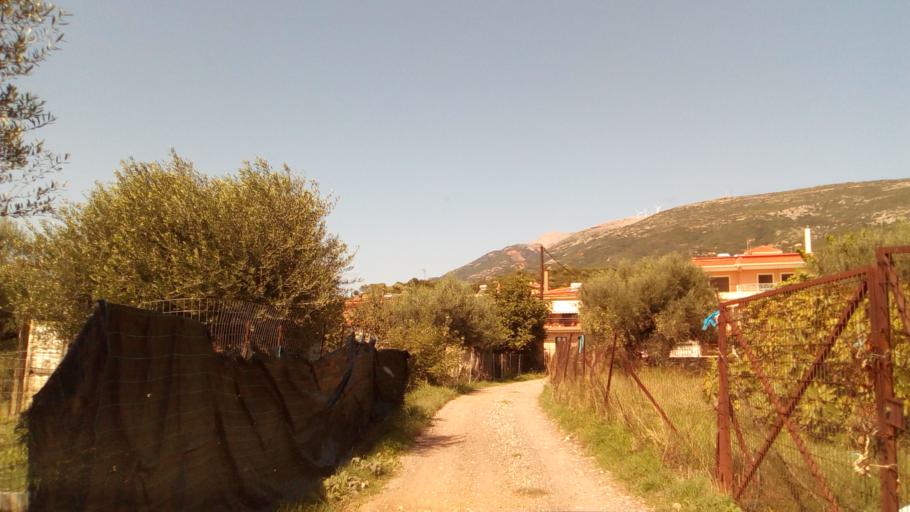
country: GR
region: West Greece
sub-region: Nomos Aitolias kai Akarnanias
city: Nafpaktos
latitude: 38.3917
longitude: 21.8148
